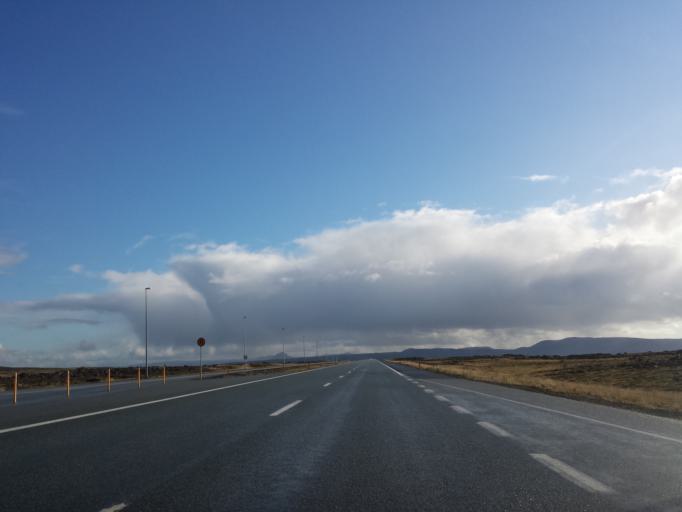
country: IS
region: Southern Peninsula
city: Vogar
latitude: 63.9634
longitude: -22.4645
